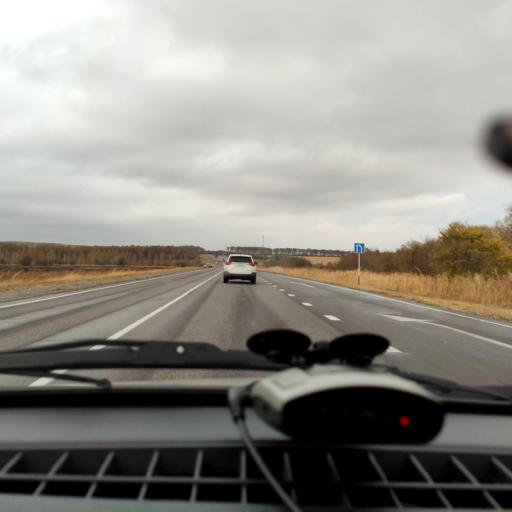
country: RU
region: Voronezj
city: Kolodeznyy
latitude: 51.3639
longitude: 39.0236
